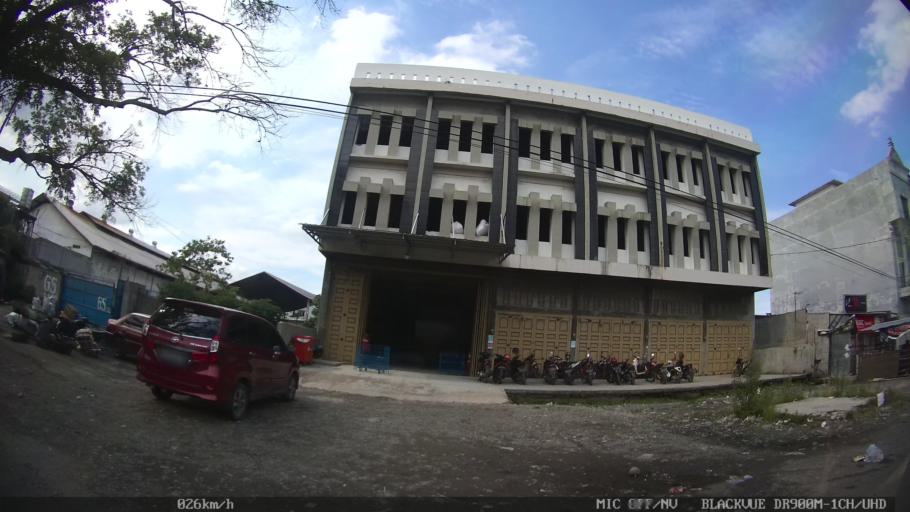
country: ID
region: North Sumatra
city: Medan
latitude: 3.6155
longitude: 98.6508
